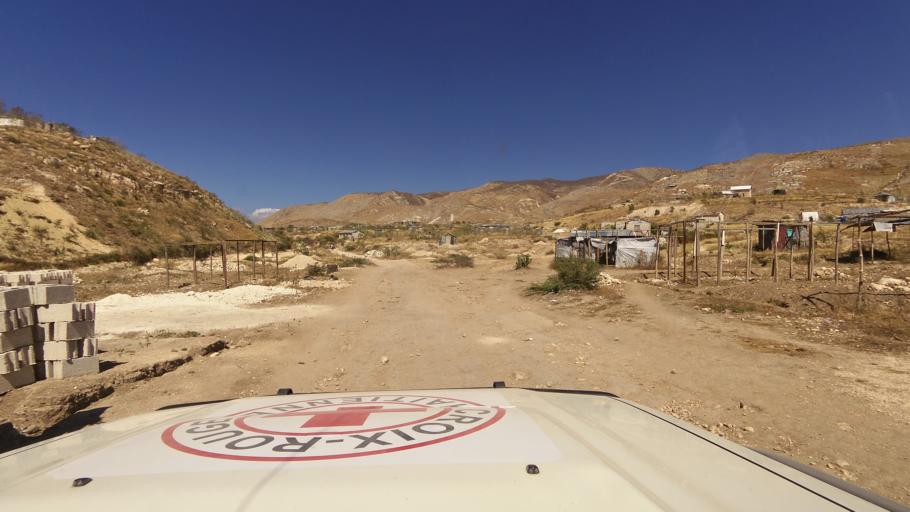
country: HT
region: Ouest
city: Croix des Bouquets
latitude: 18.6705
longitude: -72.2848
